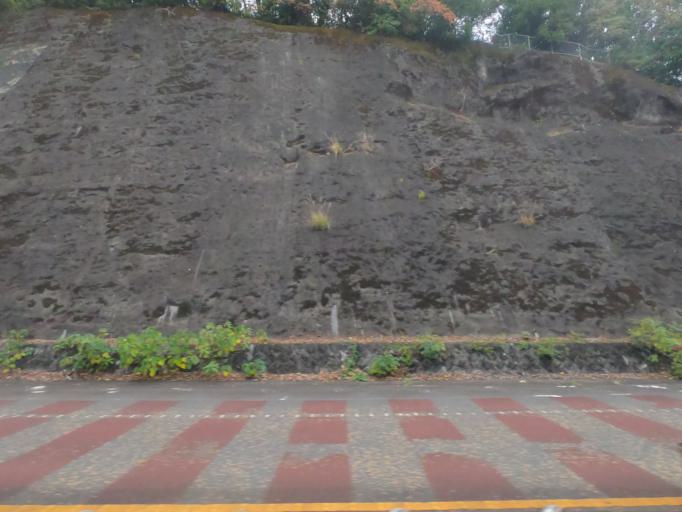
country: JP
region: Kumamoto
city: Minamata
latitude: 32.2496
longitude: 130.5025
